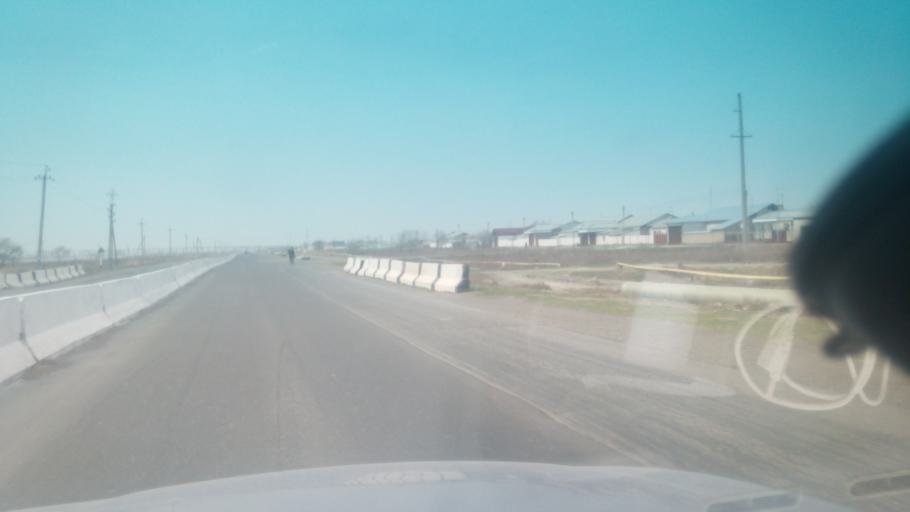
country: TJ
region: Viloyati Sughd
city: Zafarobod
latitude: 40.2216
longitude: 68.8237
